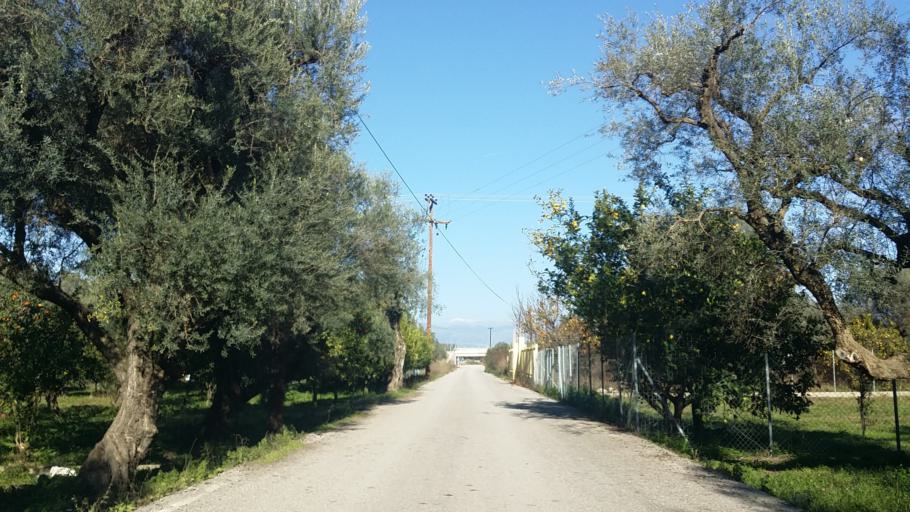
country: GR
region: West Greece
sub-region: Nomos Achaias
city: Temeni
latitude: 38.1922
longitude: 22.1818
